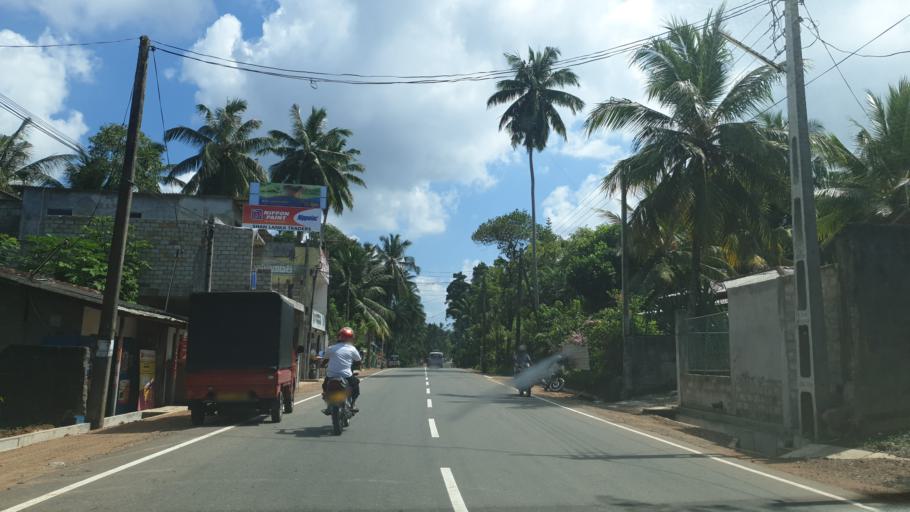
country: LK
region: Western
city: Panadura
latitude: 6.6701
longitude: 79.9415
